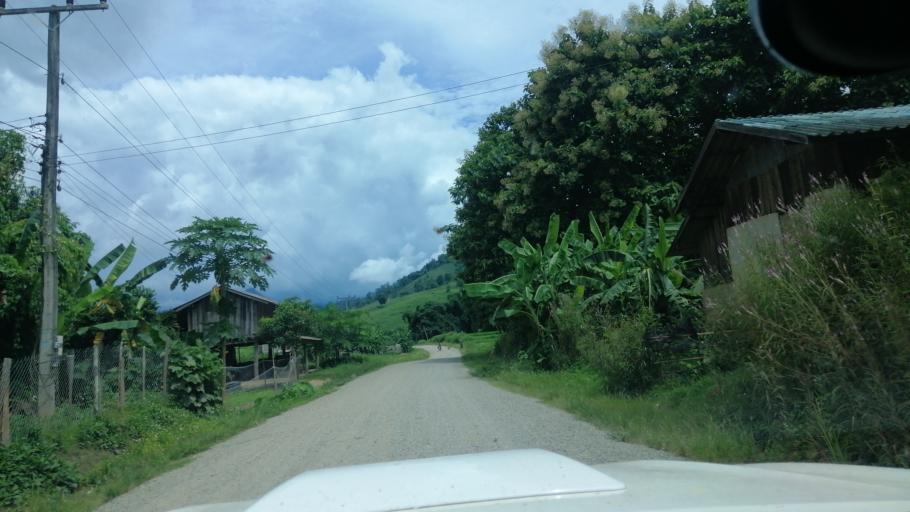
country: TH
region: Phayao
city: Phu Sang
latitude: 19.6921
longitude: 100.5015
